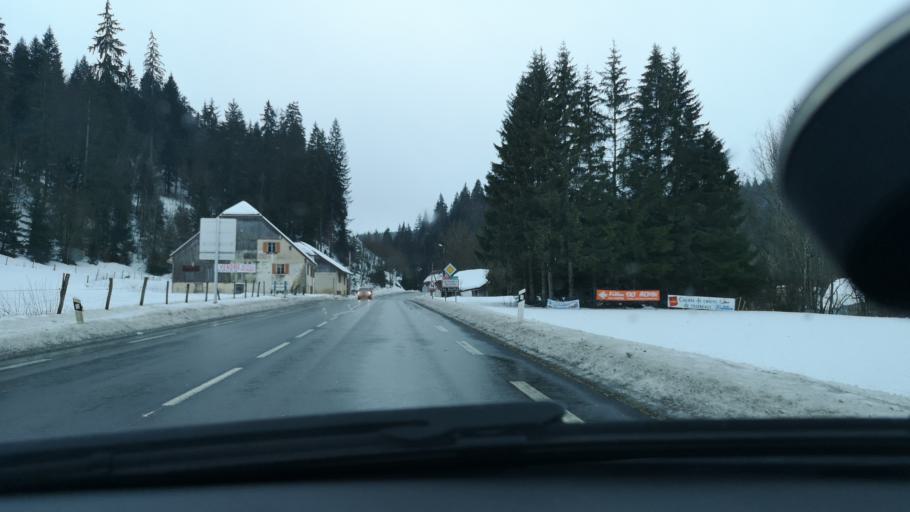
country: FR
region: Franche-Comte
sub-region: Departement du Doubs
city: La Cluse-et-Mijoux
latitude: 46.8629
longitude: 6.3721
